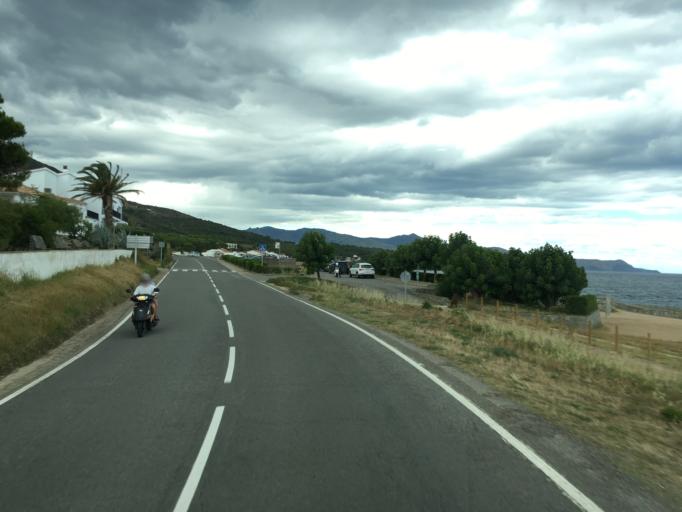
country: ES
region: Catalonia
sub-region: Provincia de Girona
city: Llanca
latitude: 42.3373
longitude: 3.1930
